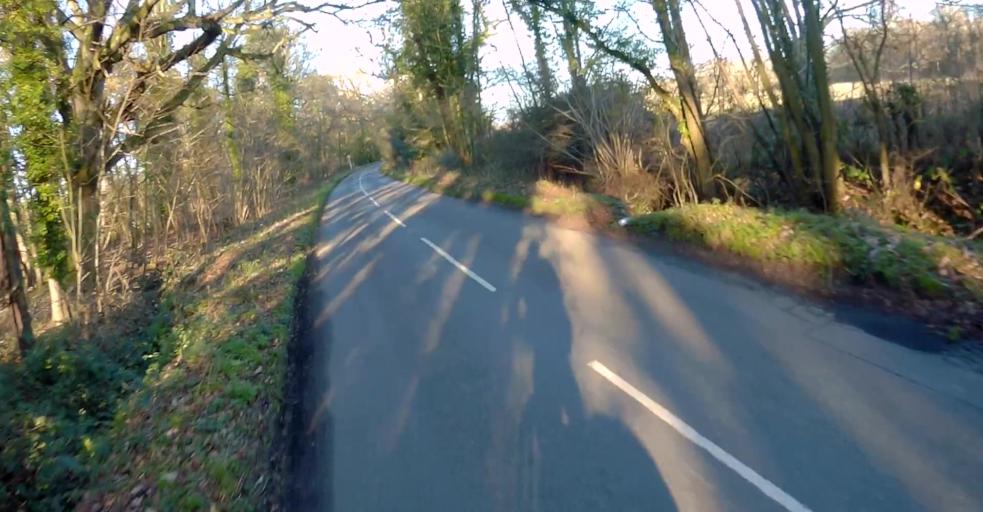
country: GB
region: England
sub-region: Hampshire
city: Hook
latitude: 51.2868
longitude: -0.9816
